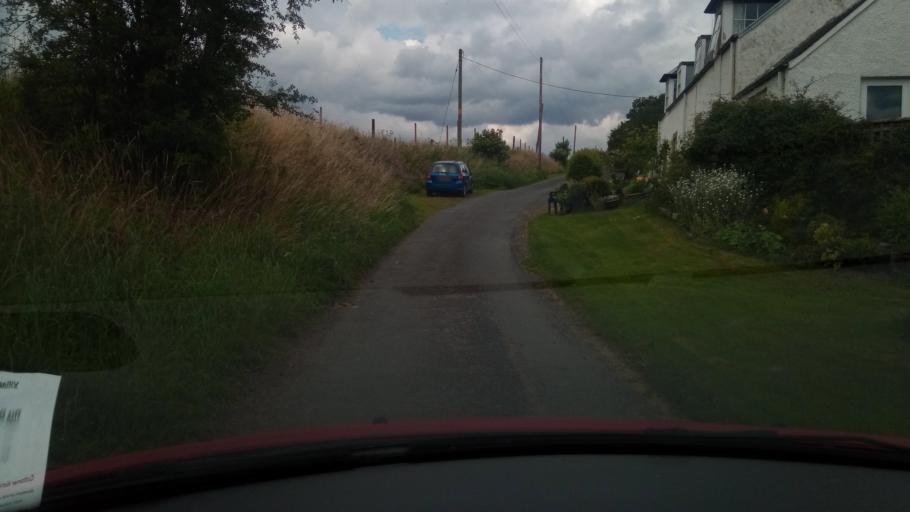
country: GB
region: Scotland
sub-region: The Scottish Borders
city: Jedburgh
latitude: 55.4293
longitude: -2.6364
